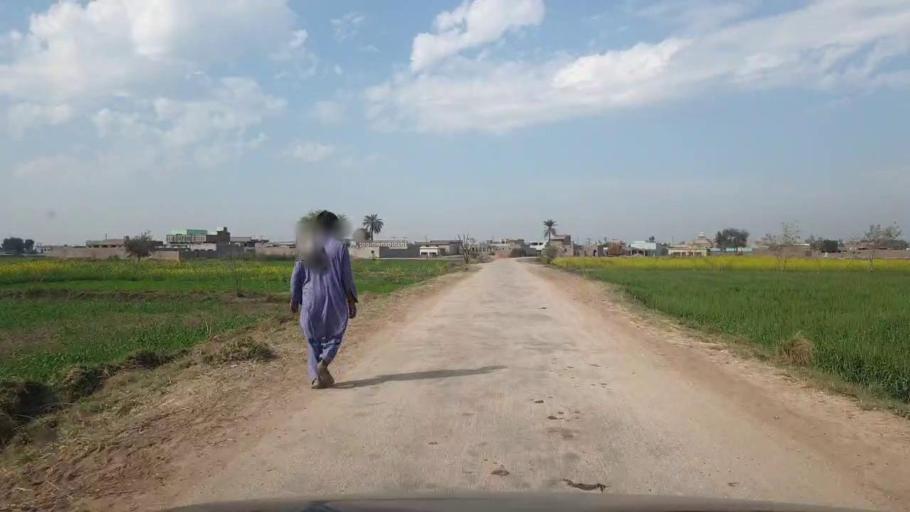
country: PK
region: Sindh
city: Sakrand
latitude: 26.0099
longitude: 68.4111
